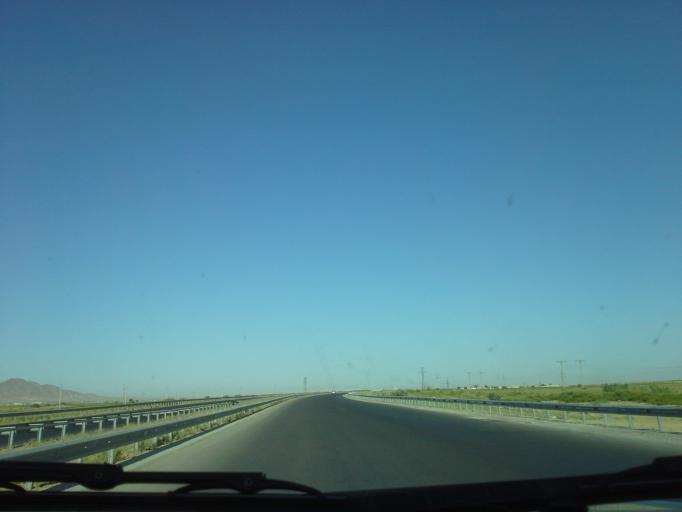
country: TM
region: Balkan
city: Gazanjyk
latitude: 39.2513
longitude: 55.5999
